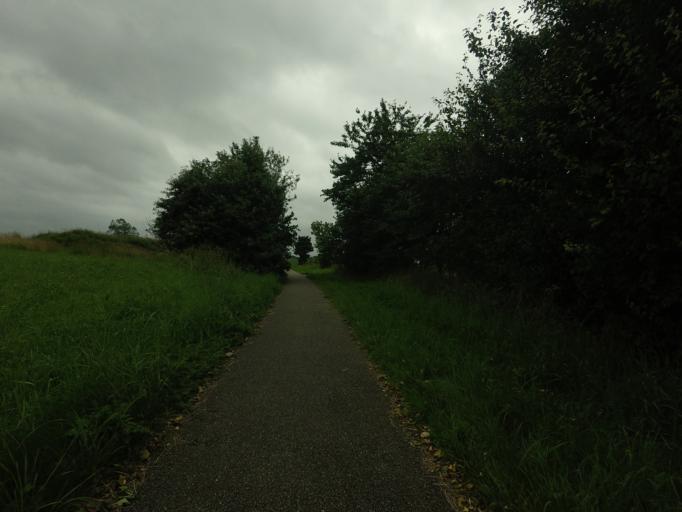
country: DK
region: Central Jutland
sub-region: Horsens Kommune
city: Braedstrup
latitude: 55.9917
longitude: 9.5890
